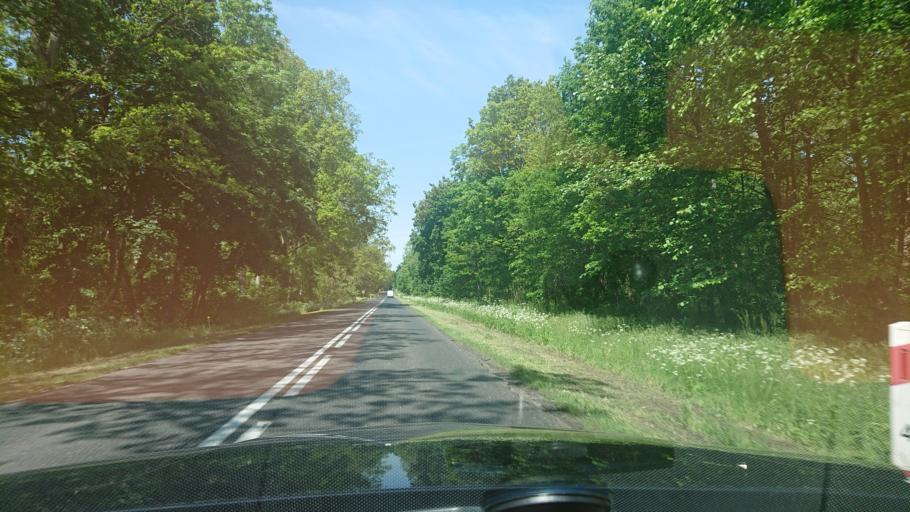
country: PL
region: Greater Poland Voivodeship
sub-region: Powiat gnieznienski
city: Gniezno
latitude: 52.5017
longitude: 17.6312
